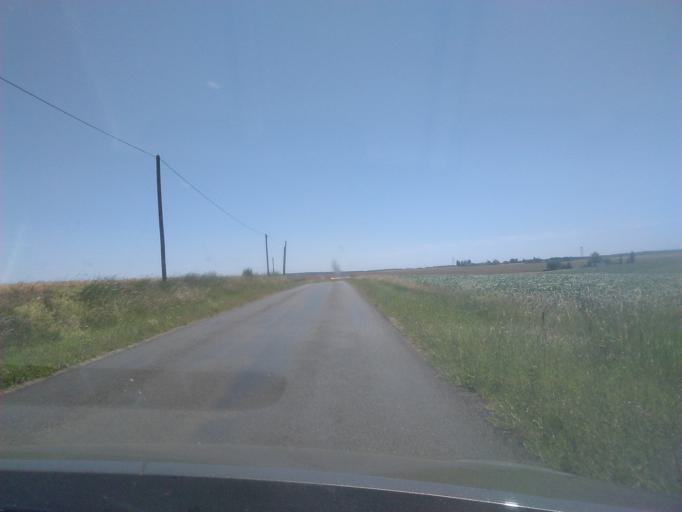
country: FR
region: Centre
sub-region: Departement du Loir-et-Cher
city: Herbault
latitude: 47.6448
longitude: 1.1928
